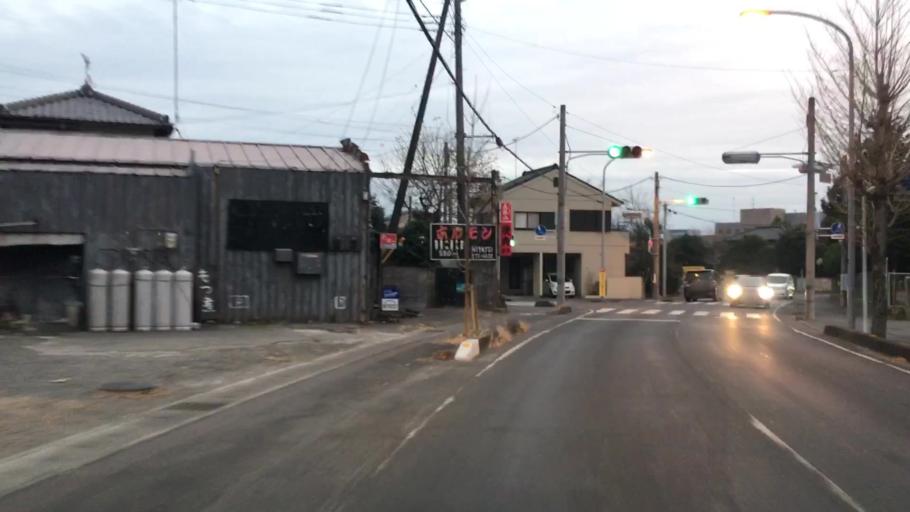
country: JP
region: Gunma
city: Ota
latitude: 36.3009
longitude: 139.3667
